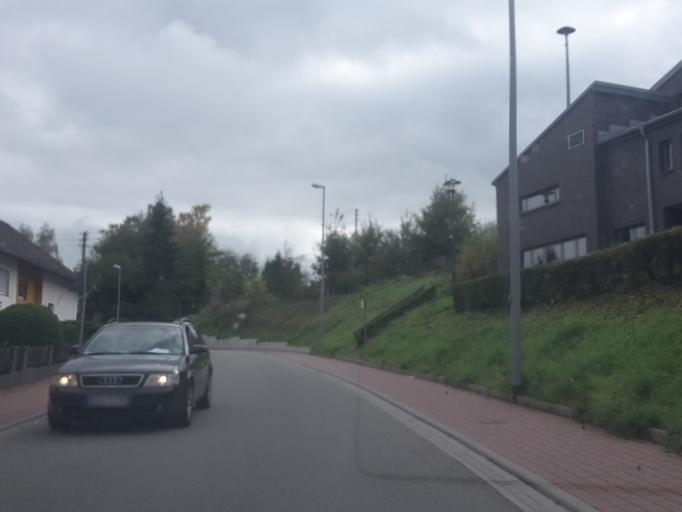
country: DE
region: Hesse
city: Bad Camberg
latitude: 50.2673
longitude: 8.2341
